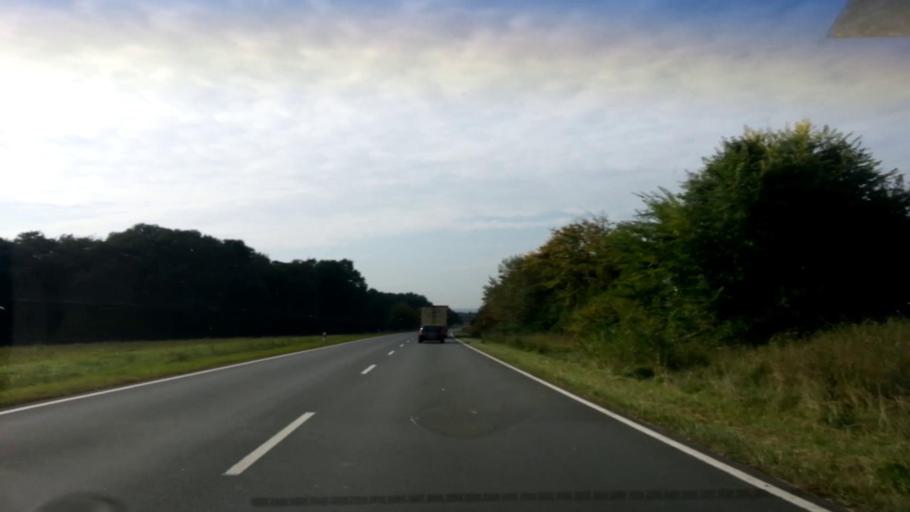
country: DE
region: Bavaria
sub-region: Regierungsbezirk Unterfranken
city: Wiesentheid
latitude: 49.8044
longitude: 10.3599
